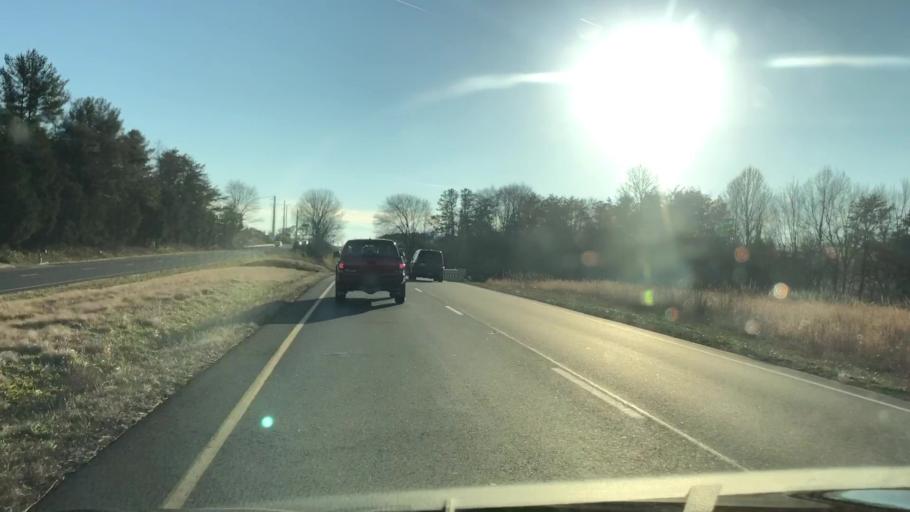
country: US
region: Virginia
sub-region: Greene County
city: Ruckersville
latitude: 38.2123
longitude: -78.3833
